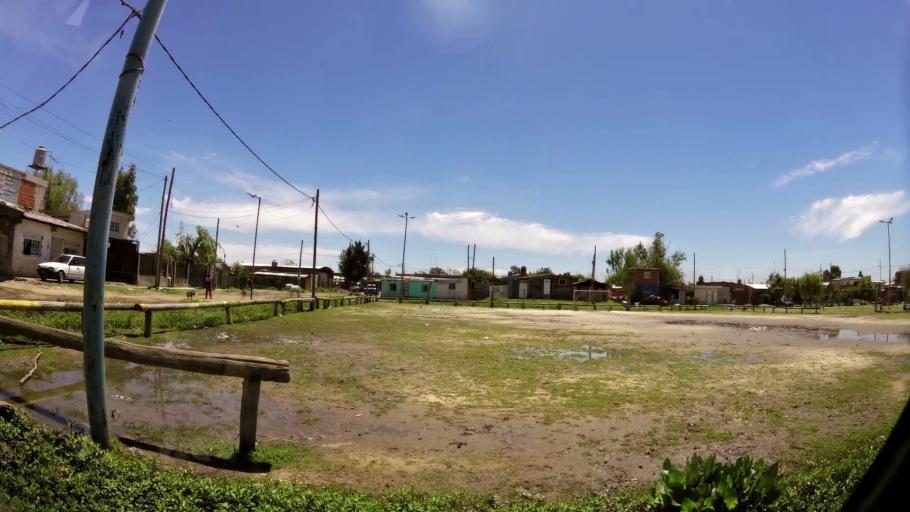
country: AR
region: Buenos Aires
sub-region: Partido de Quilmes
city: Quilmes
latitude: -34.7440
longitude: -58.3065
